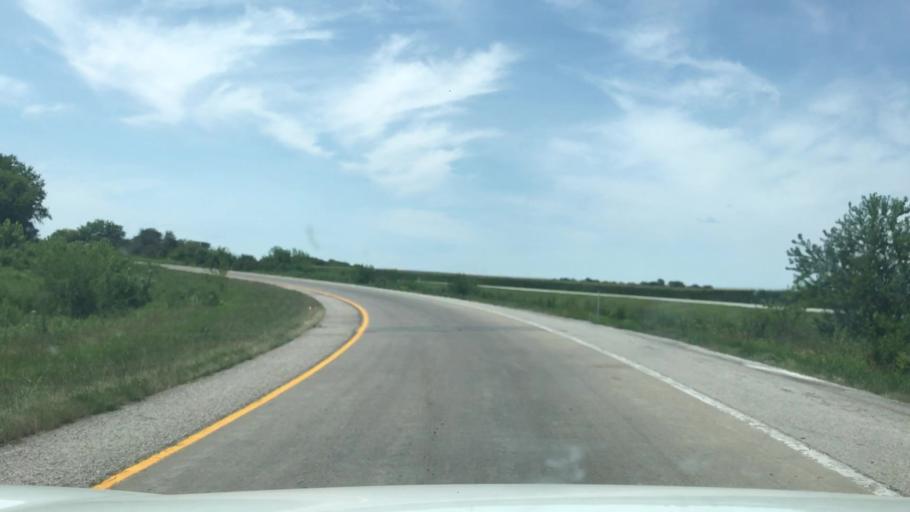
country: US
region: Illinois
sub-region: Clinton County
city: New Baden
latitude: 38.5365
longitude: -89.7266
